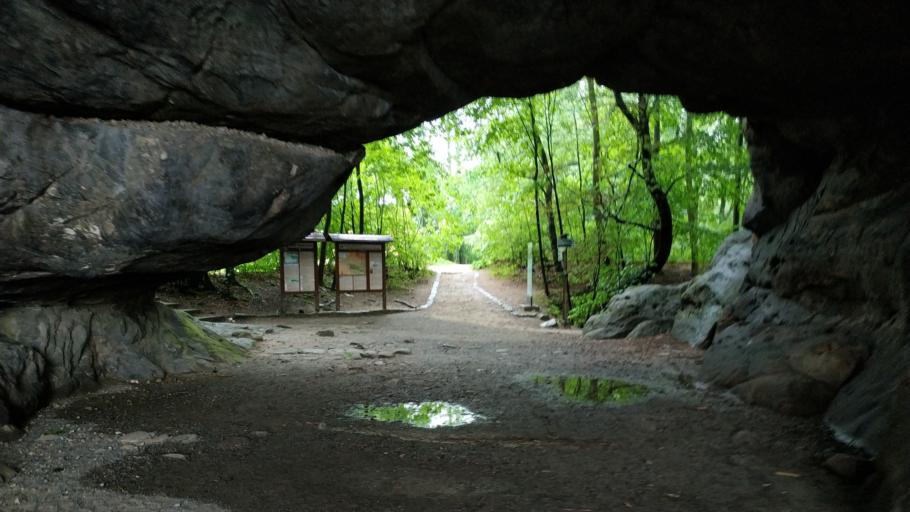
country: DE
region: Saxony
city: Sebnitz
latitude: 50.9257
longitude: 14.2571
